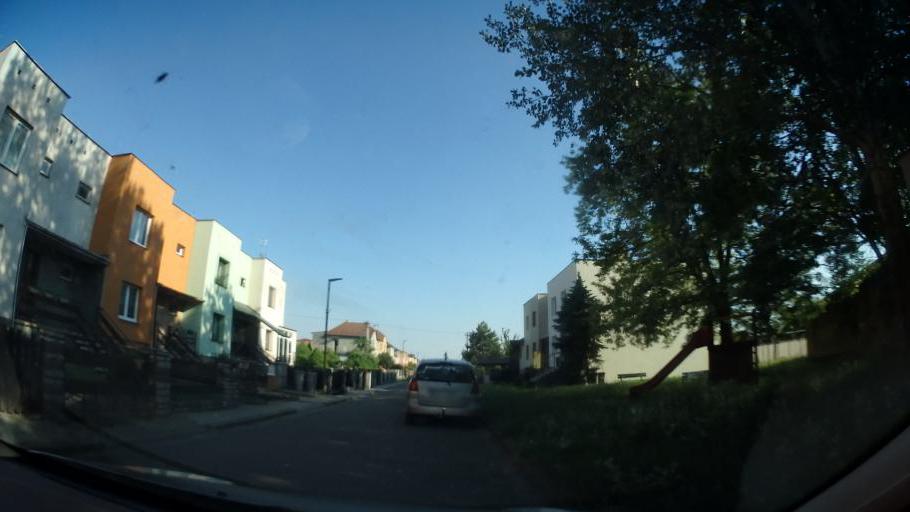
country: CZ
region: Zlin
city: Chropyne
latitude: 49.3678
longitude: 17.3595
